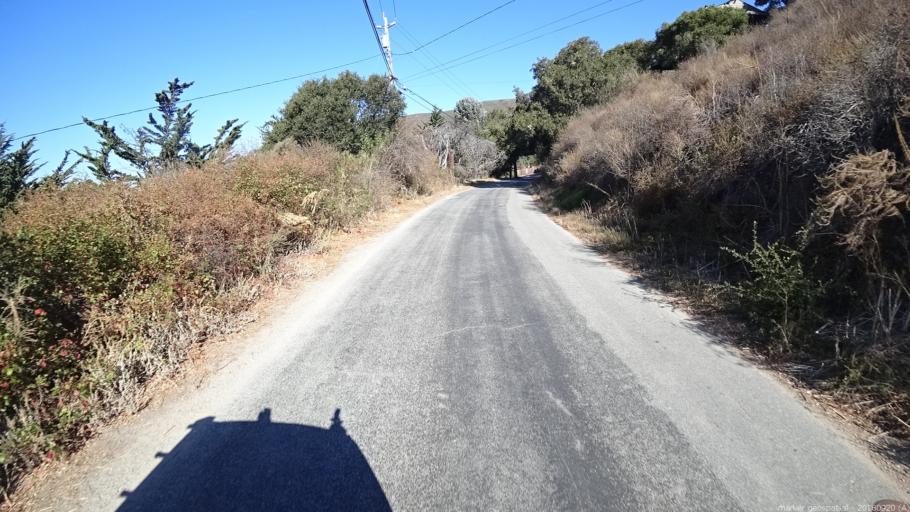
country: US
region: California
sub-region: Monterey County
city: Carmel Valley Village
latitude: 36.5208
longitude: -121.7905
